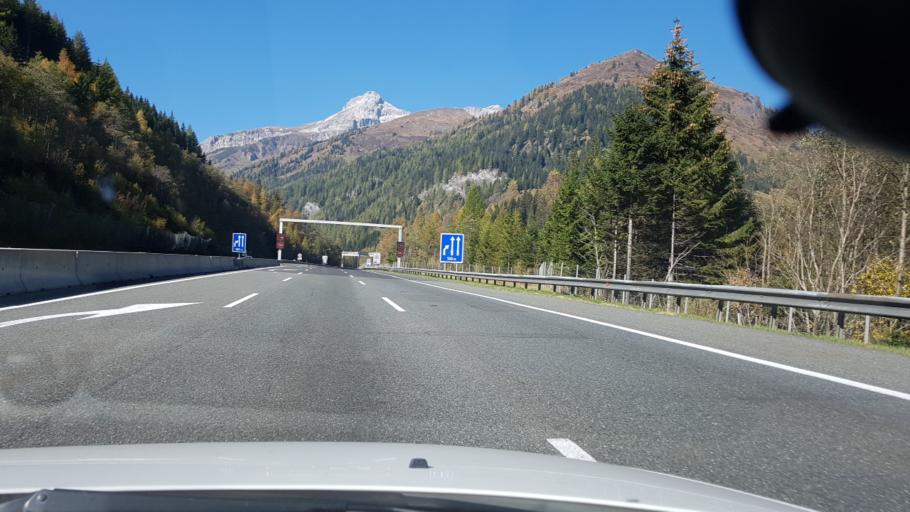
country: AT
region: Salzburg
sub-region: Politischer Bezirk Tamsweg
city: Zederhaus
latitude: 47.1779
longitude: 13.4442
